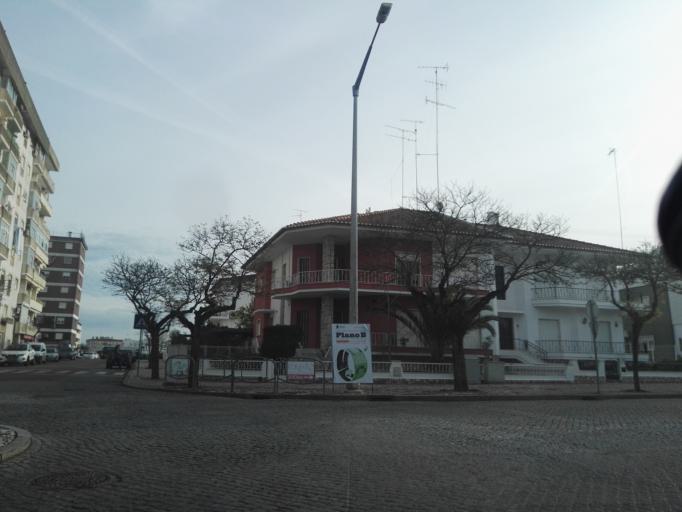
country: PT
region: Portalegre
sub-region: Elvas
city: Elvas
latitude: 38.8756
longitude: -7.1734
